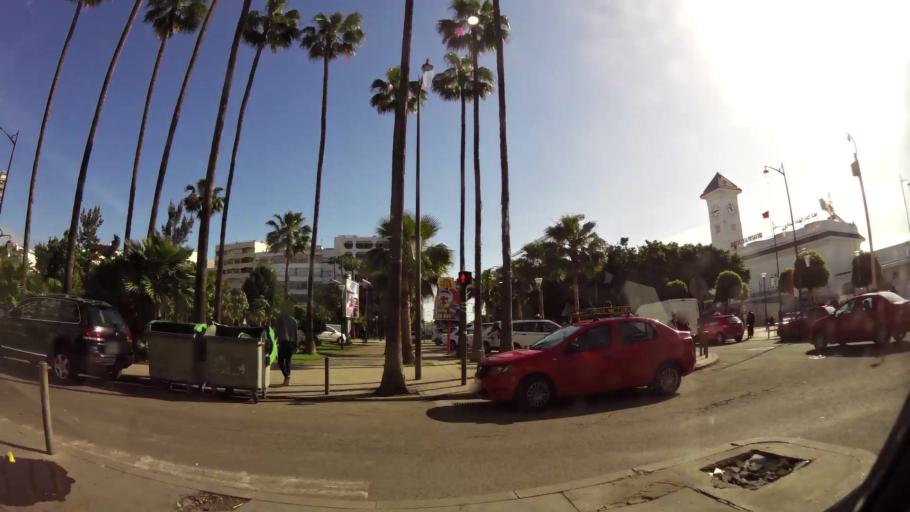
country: MA
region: Grand Casablanca
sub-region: Casablanca
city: Casablanca
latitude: 33.5897
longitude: -7.5920
